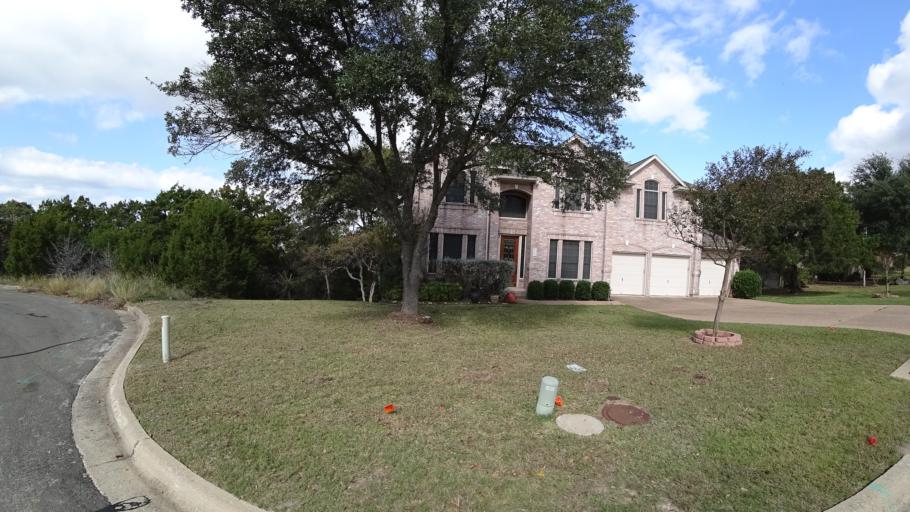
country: US
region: Texas
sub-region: Williamson County
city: Jollyville
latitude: 30.4145
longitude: -97.7911
